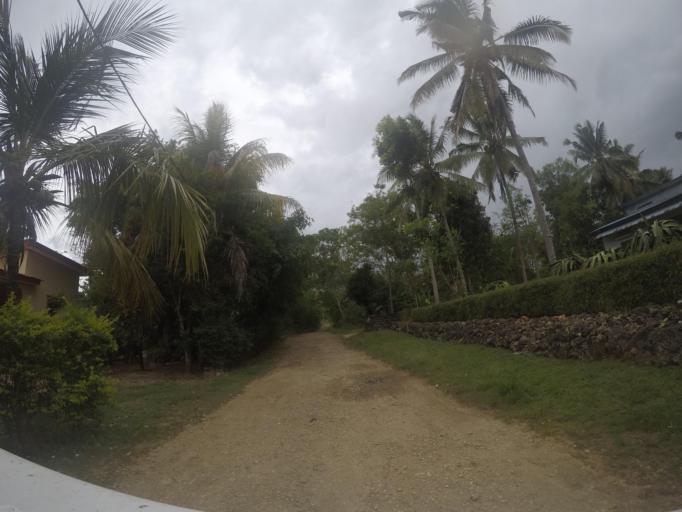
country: TL
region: Lautem
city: Lospalos
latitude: -8.5257
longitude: 126.9938
